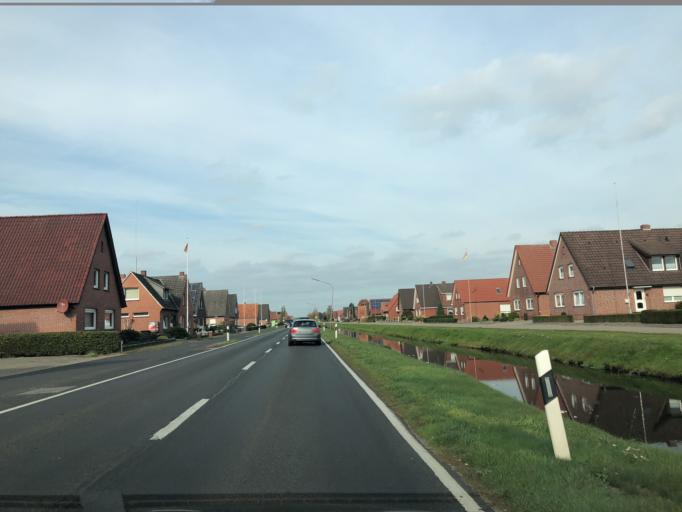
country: DE
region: Lower Saxony
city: Papenburg
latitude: 53.0457
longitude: 7.4632
